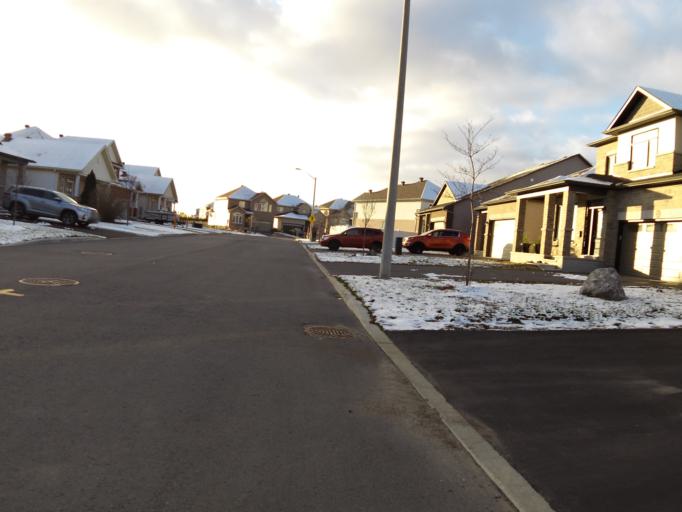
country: CA
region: Ontario
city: Ottawa
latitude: 45.4243
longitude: -75.5182
